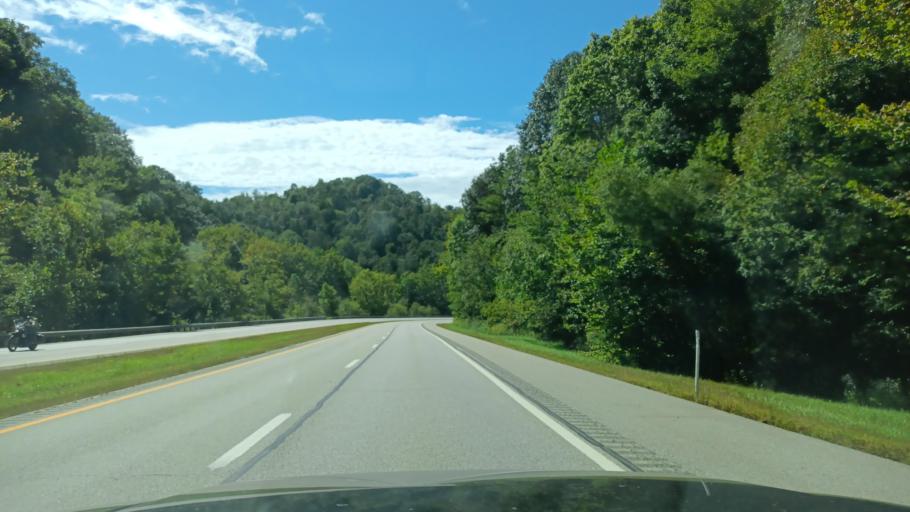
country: US
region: West Virginia
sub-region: Harrison County
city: Salem
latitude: 39.2870
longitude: -80.6452
